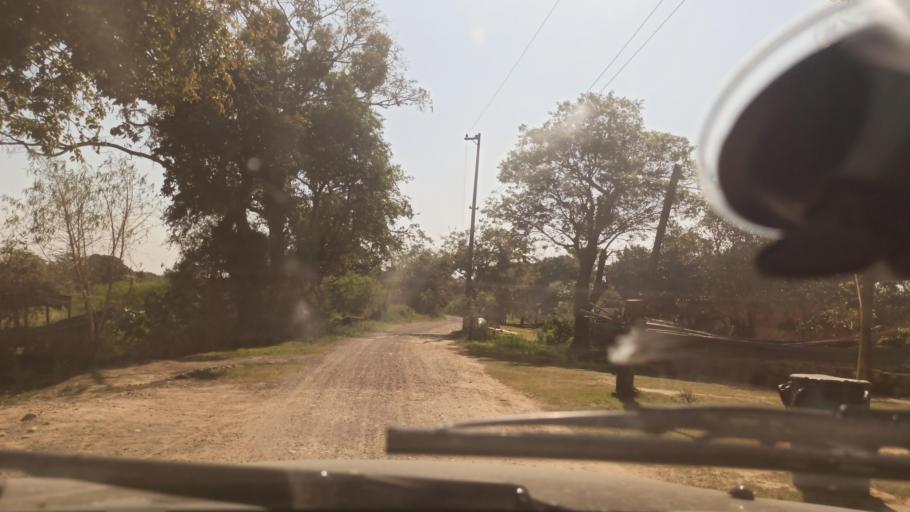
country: AR
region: Formosa
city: Clorinda
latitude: -25.3299
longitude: -57.6907
